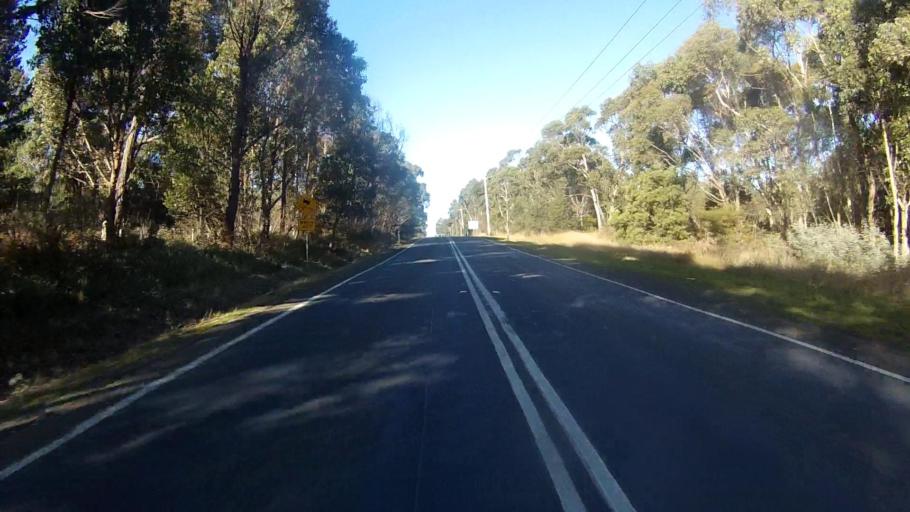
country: AU
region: Tasmania
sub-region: Sorell
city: Sorell
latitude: -42.8199
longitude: 147.8015
